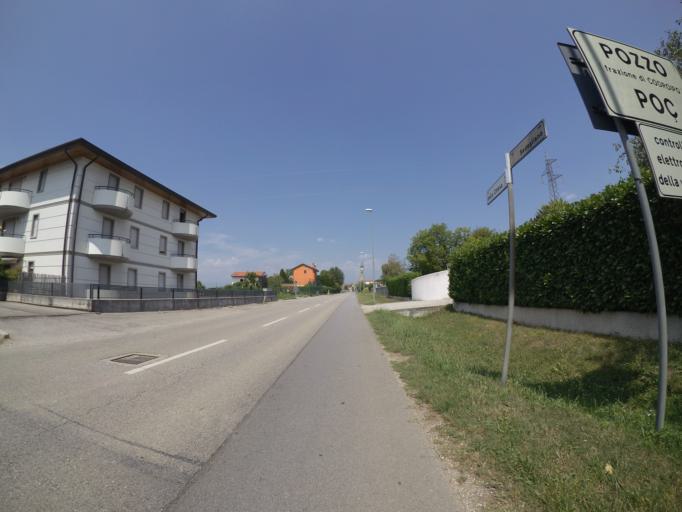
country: IT
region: Friuli Venezia Giulia
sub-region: Provincia di Udine
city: Codroipo
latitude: 45.9823
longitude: 12.9713
